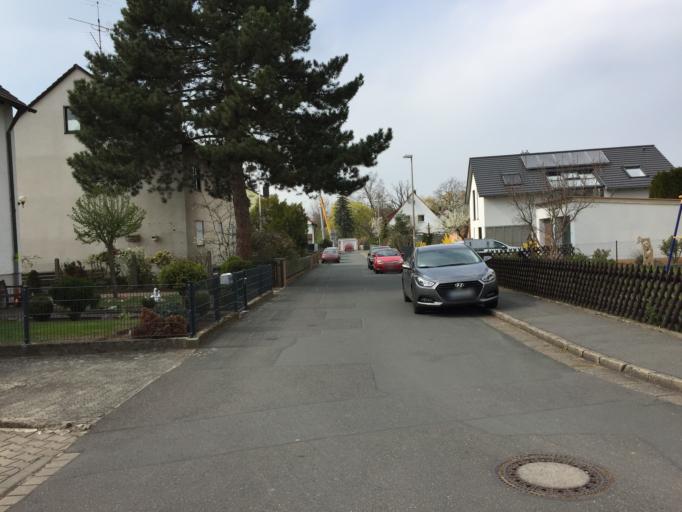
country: DE
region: Bavaria
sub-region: Regierungsbezirk Mittelfranken
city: Erlangen
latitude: 49.5671
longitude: 10.9660
